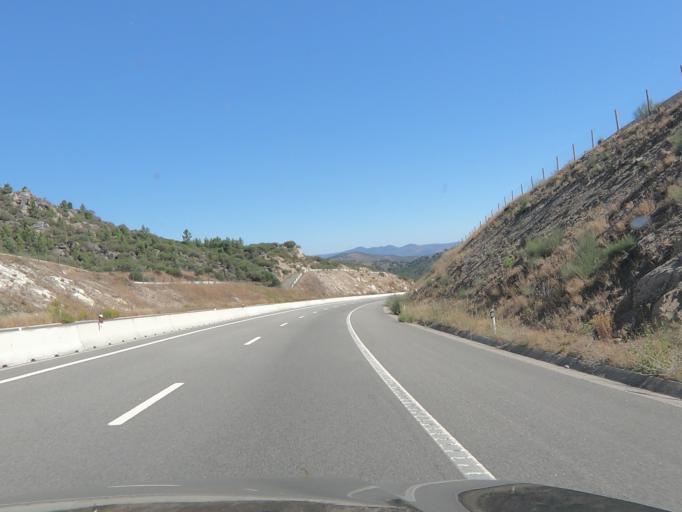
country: PT
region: Vila Real
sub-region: Murca
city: Murca
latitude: 41.3894
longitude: -7.4723
